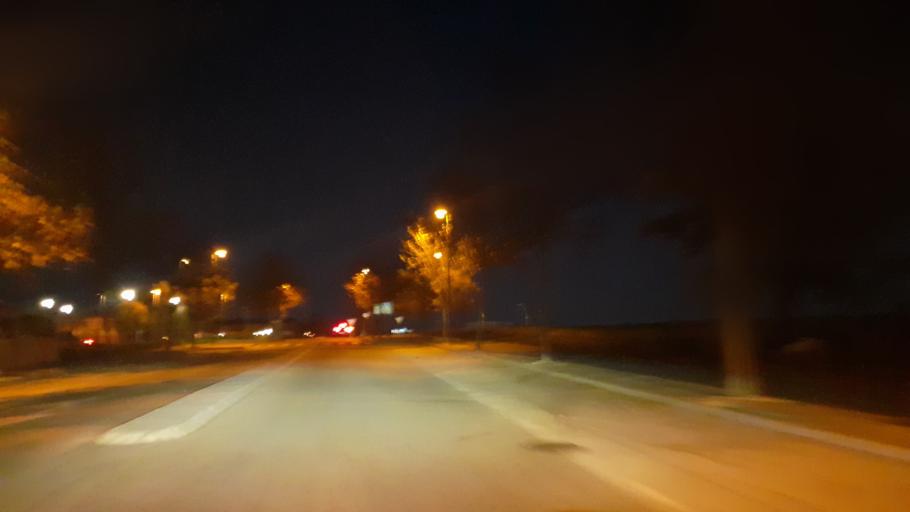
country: ES
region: Madrid
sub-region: Provincia de Madrid
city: Paracuellos de Jarama
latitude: 40.5096
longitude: -3.5125
